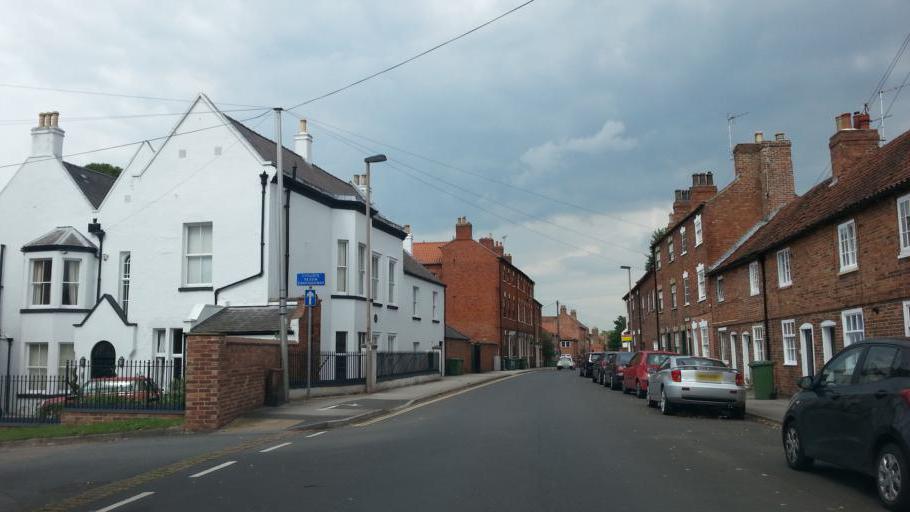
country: GB
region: England
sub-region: Nottinghamshire
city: Newark on Trent
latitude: 53.0729
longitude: -0.8187
